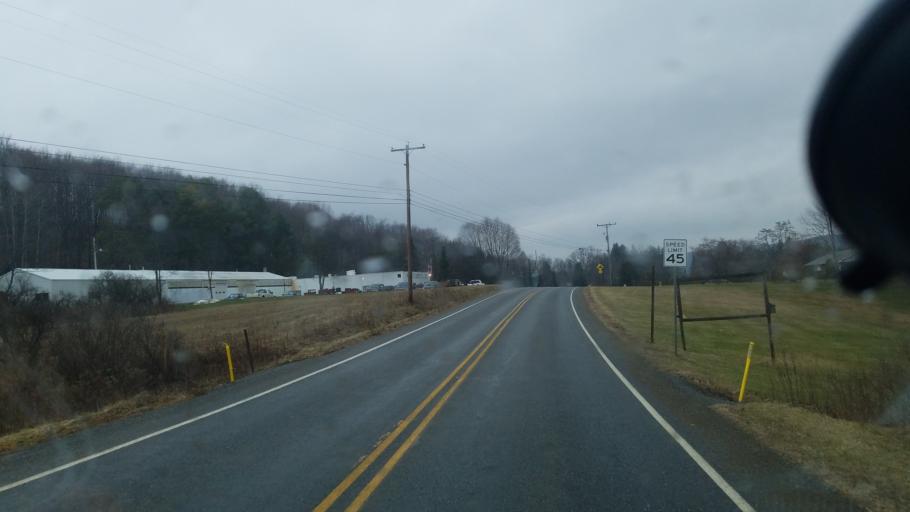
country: US
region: New York
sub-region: Allegany County
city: Wellsville
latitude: 41.9837
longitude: -77.8665
